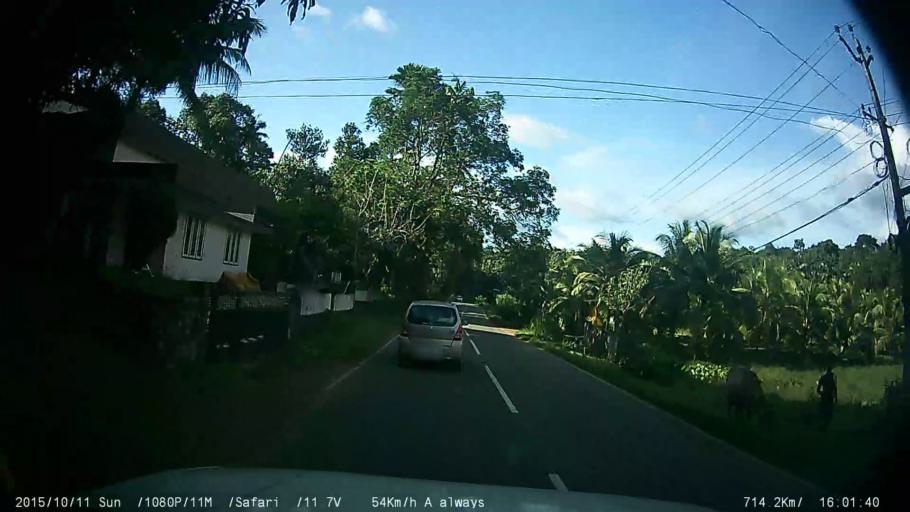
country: IN
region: Kerala
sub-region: Kottayam
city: Palackattumala
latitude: 9.6588
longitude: 76.6122
